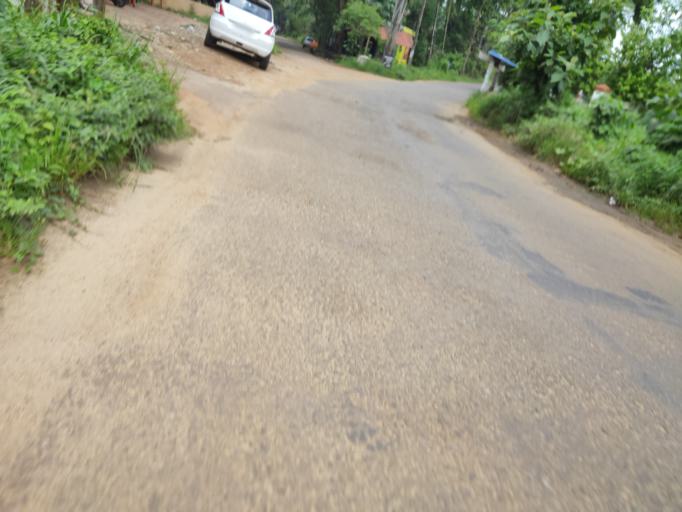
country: IN
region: Kerala
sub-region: Malappuram
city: Manjeri
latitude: 11.2332
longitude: 76.2840
